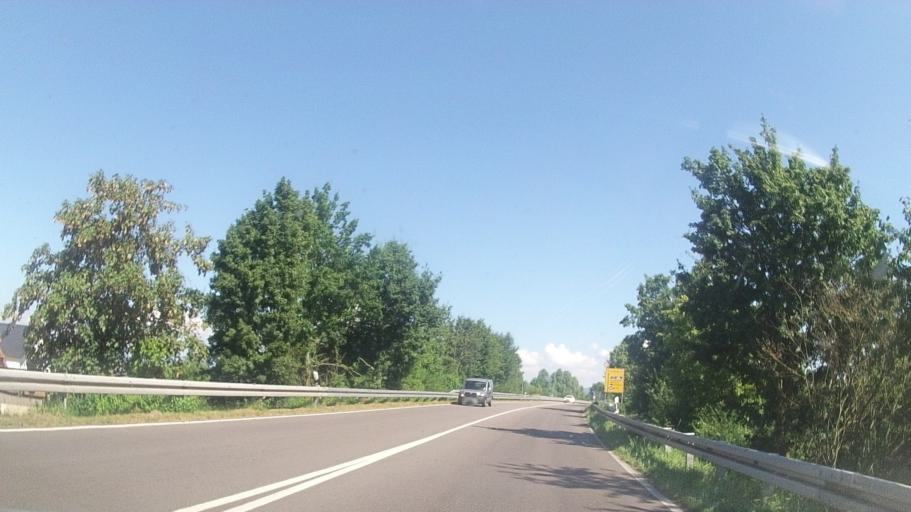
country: DE
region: Baden-Wuerttemberg
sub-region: Freiburg Region
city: Willstatt
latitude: 48.5352
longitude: 7.9196
